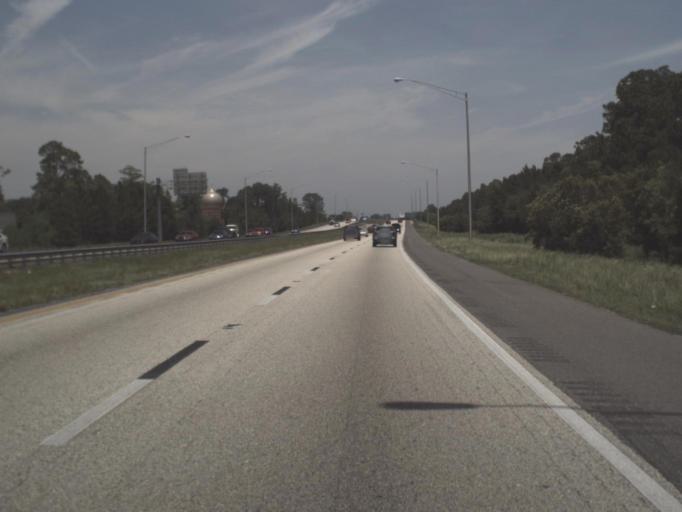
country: US
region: Florida
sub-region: Duval County
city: Neptune Beach
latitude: 30.3039
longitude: -81.5235
